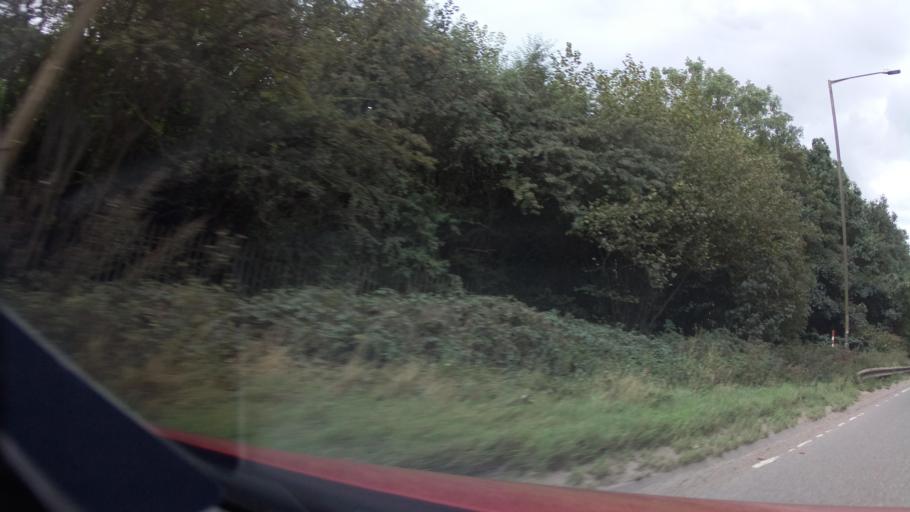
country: GB
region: England
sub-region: Warwickshire
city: Curdworth
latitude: 52.5348
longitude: -1.7234
